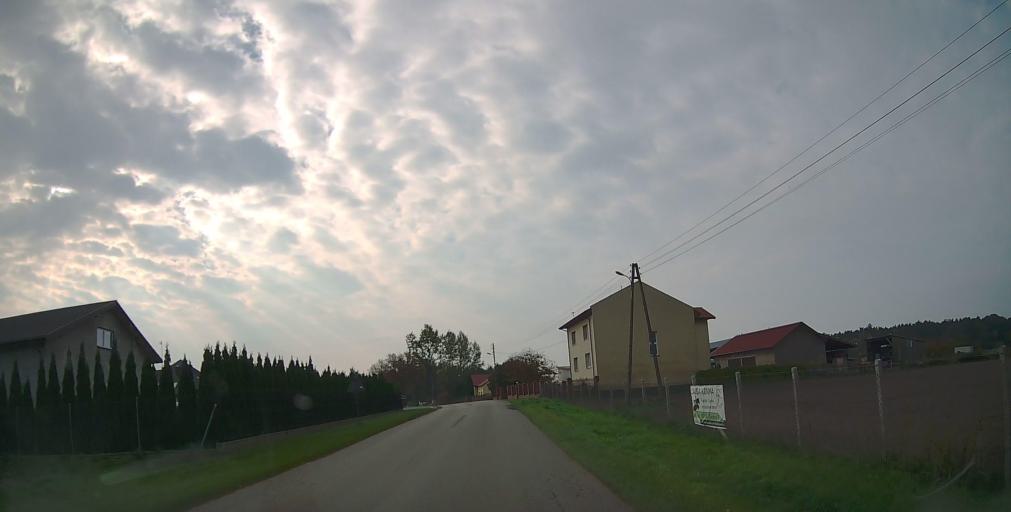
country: PL
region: Masovian Voivodeship
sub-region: Powiat grojecki
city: Mogielnica
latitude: 51.6669
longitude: 20.7111
